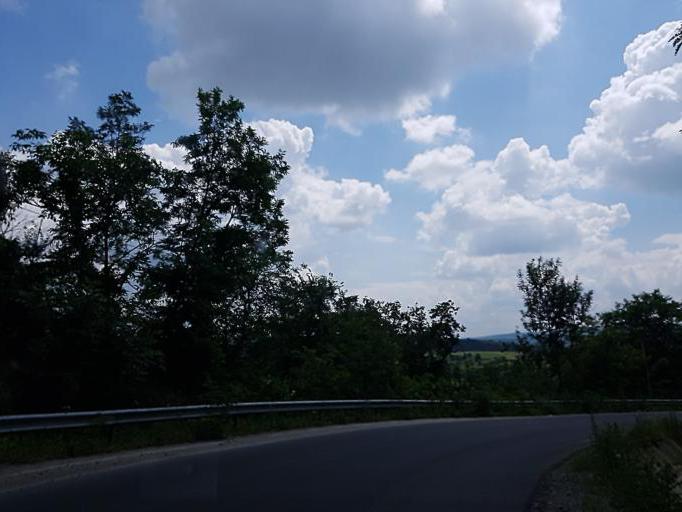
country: RO
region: Sibiu
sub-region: Comuna Seica Mare
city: Seica Mare
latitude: 46.0348
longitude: 24.1604
